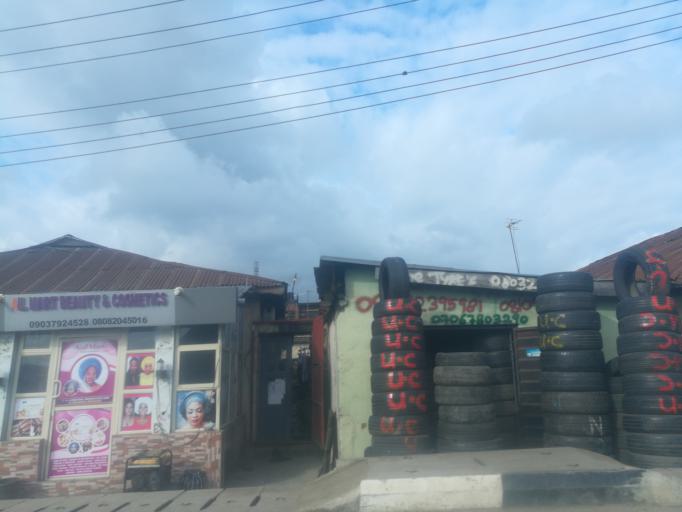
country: NG
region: Lagos
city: Somolu
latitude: 6.5400
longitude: 3.3813
